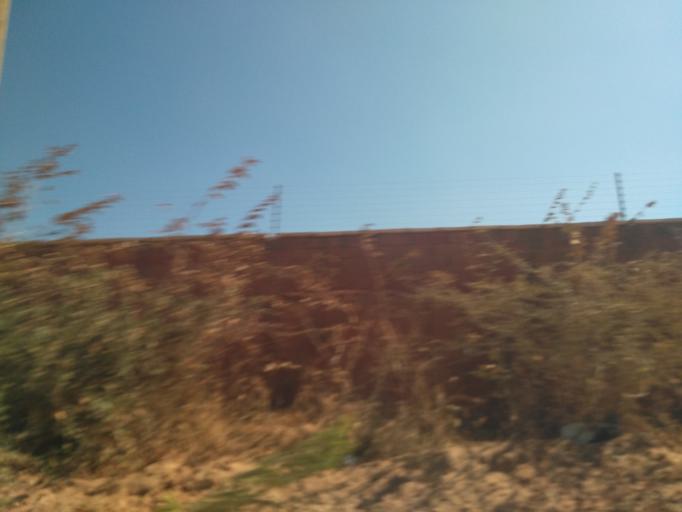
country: TZ
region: Dodoma
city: Dodoma
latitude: -6.1672
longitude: 35.7029
